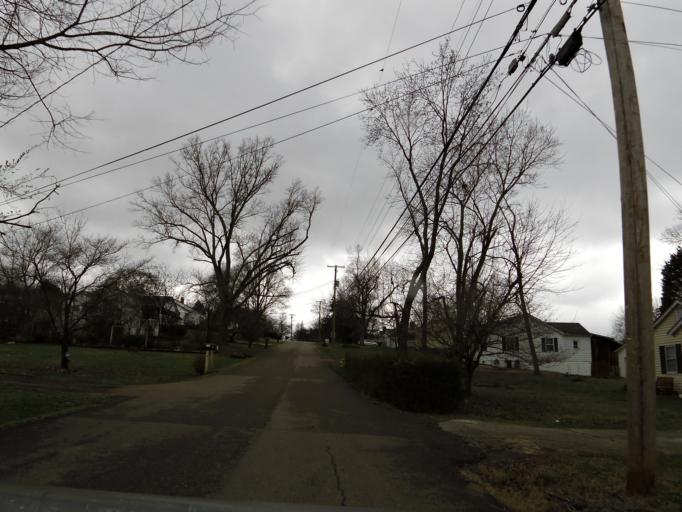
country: US
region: Tennessee
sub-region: Knox County
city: Knoxville
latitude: 35.9988
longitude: -83.9763
